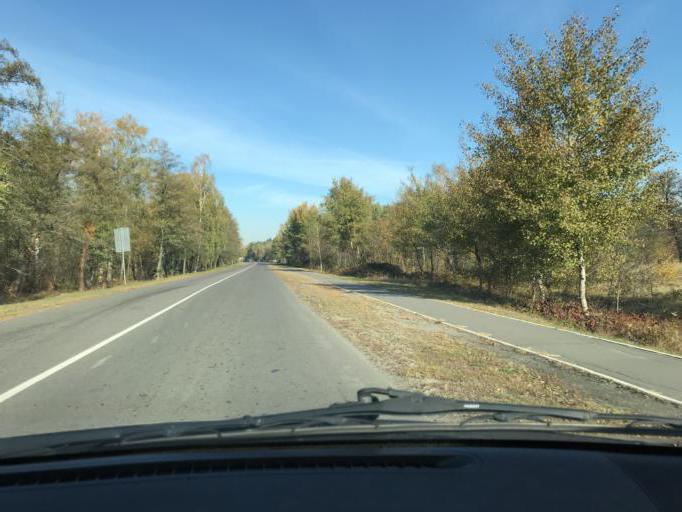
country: BY
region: Brest
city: Mikashevichy
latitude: 52.2329
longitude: 27.4493
